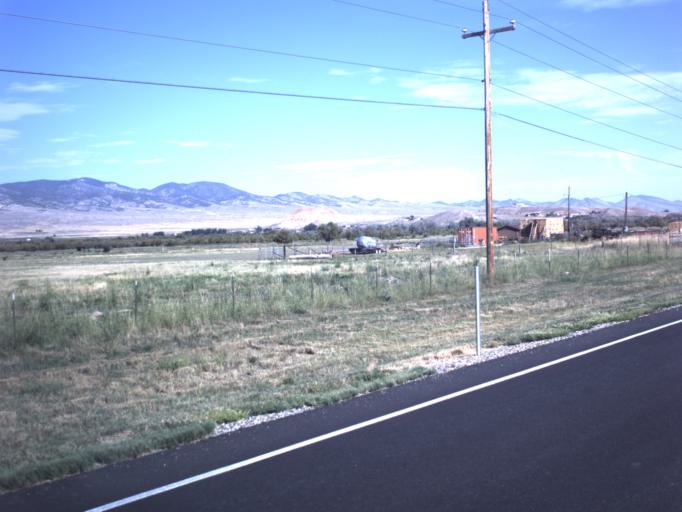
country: US
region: Utah
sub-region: Sevier County
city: Salina
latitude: 38.9831
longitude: -111.8606
